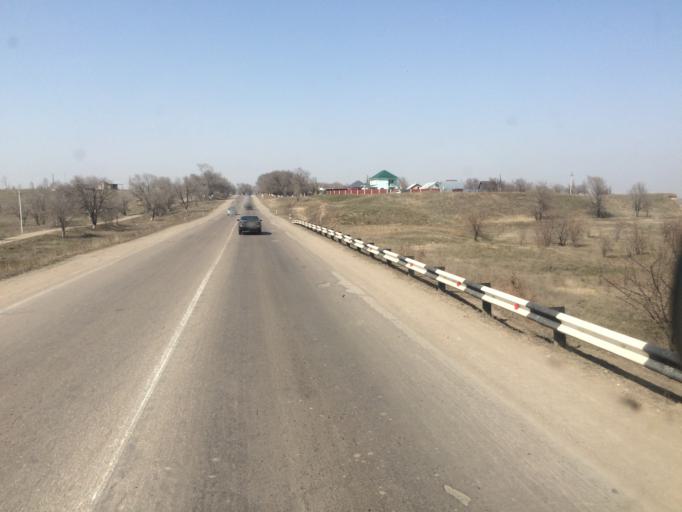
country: KZ
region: Almaty Oblysy
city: Burunday
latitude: 43.3046
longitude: 76.6709
